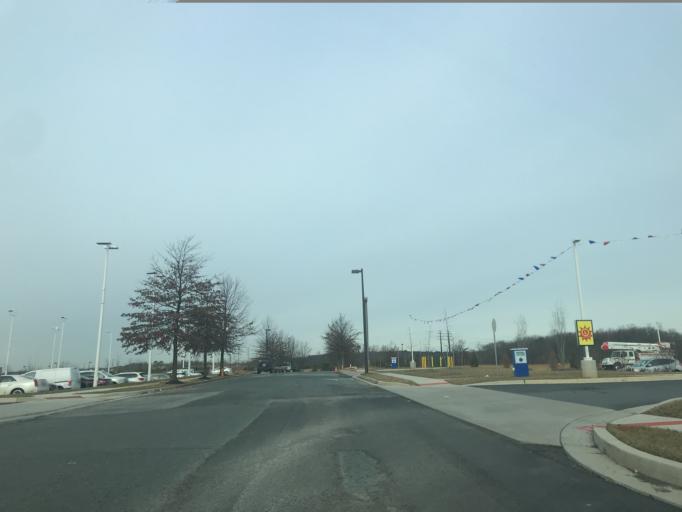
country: US
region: Maryland
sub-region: Baltimore County
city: White Marsh
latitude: 39.3731
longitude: -76.4424
